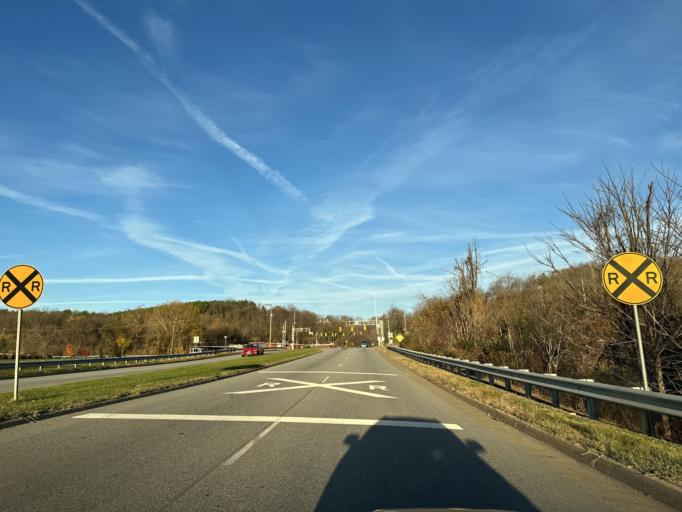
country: US
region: Virginia
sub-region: City of Staunton
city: Staunton
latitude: 38.1530
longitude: -79.0555
